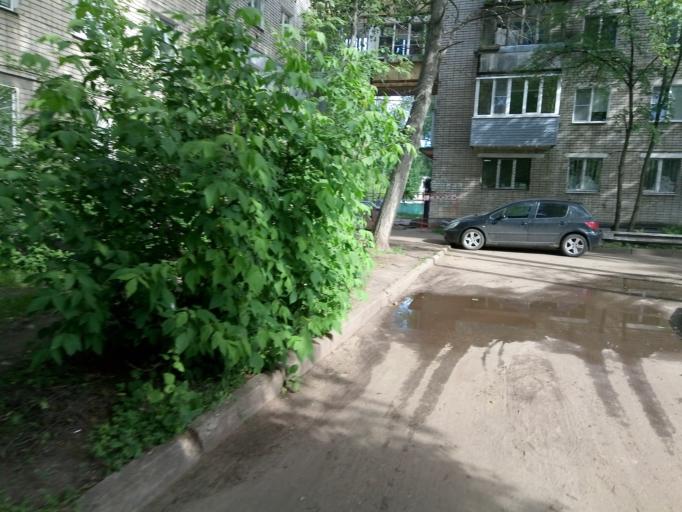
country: RU
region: Jaroslavl
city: Yaroslavl
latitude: 57.6504
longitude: 39.9426
